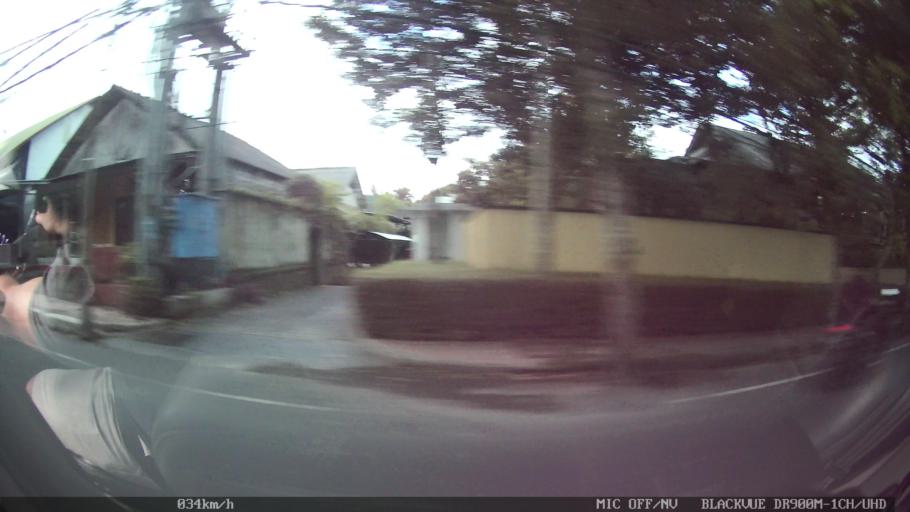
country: ID
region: Bali
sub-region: Kabupaten Gianyar
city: Ubud
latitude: -8.4916
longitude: 115.2536
